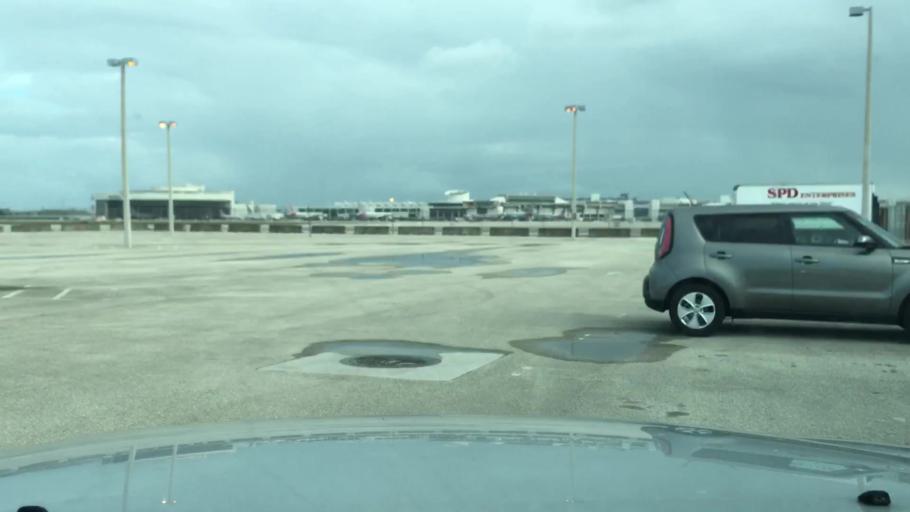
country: US
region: Florida
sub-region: Miami-Dade County
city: Miami Springs
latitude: 25.8063
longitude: -80.2766
